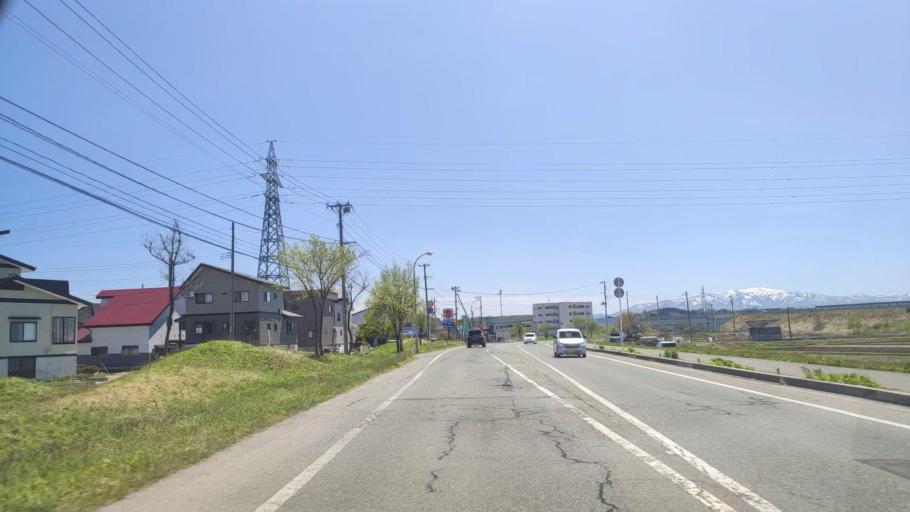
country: JP
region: Yamagata
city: Shinjo
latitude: 38.7483
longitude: 140.2955
